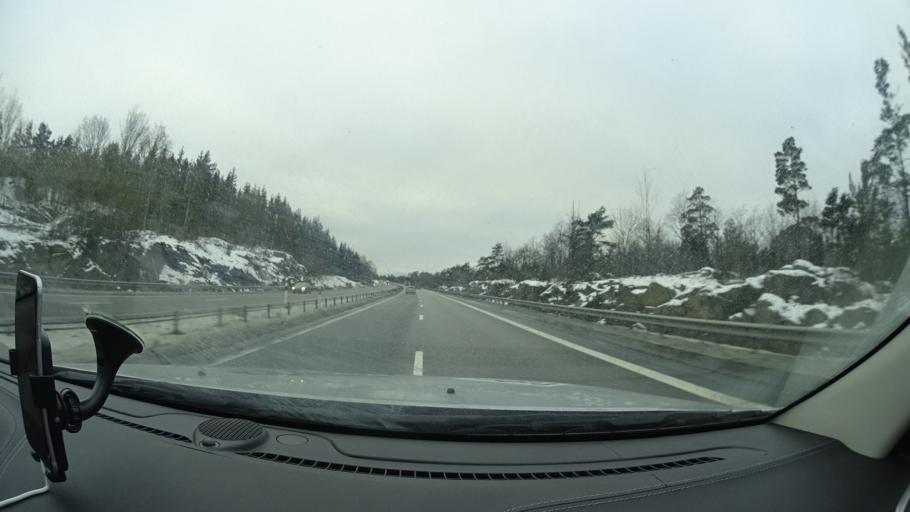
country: SE
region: Joenkoeping
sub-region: Jonkopings Kommun
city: Kaxholmen
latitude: 57.9652
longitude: 14.3614
